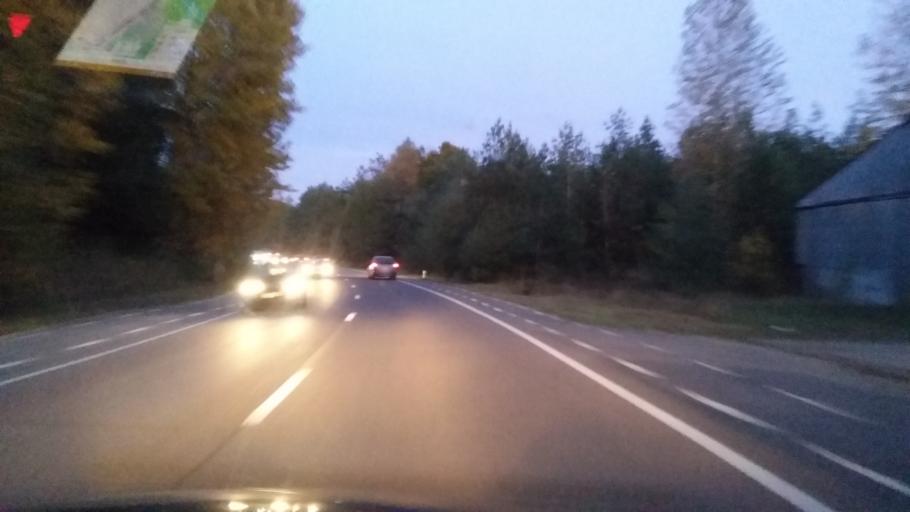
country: BE
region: Wallonia
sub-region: Province du Luxembourg
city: Saint-Leger
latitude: 49.6730
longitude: 5.6943
